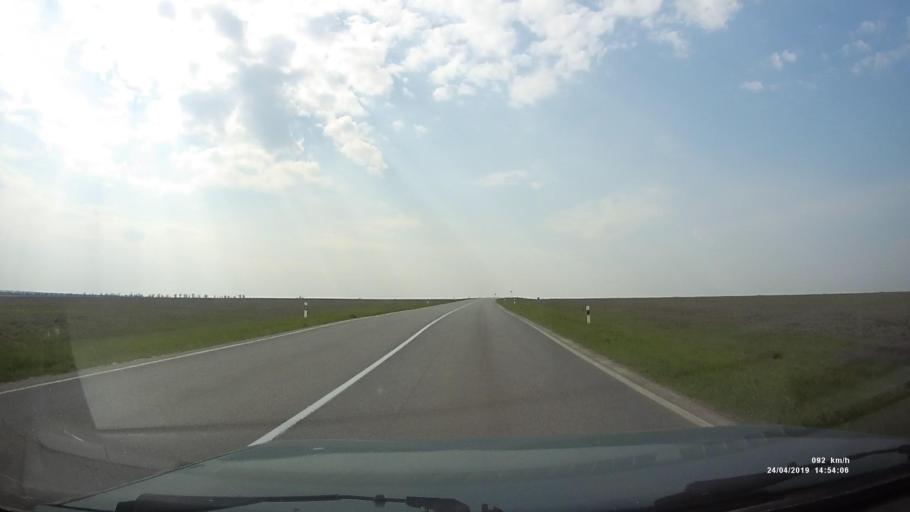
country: RU
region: Rostov
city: Remontnoye
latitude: 46.5325
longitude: 43.6451
